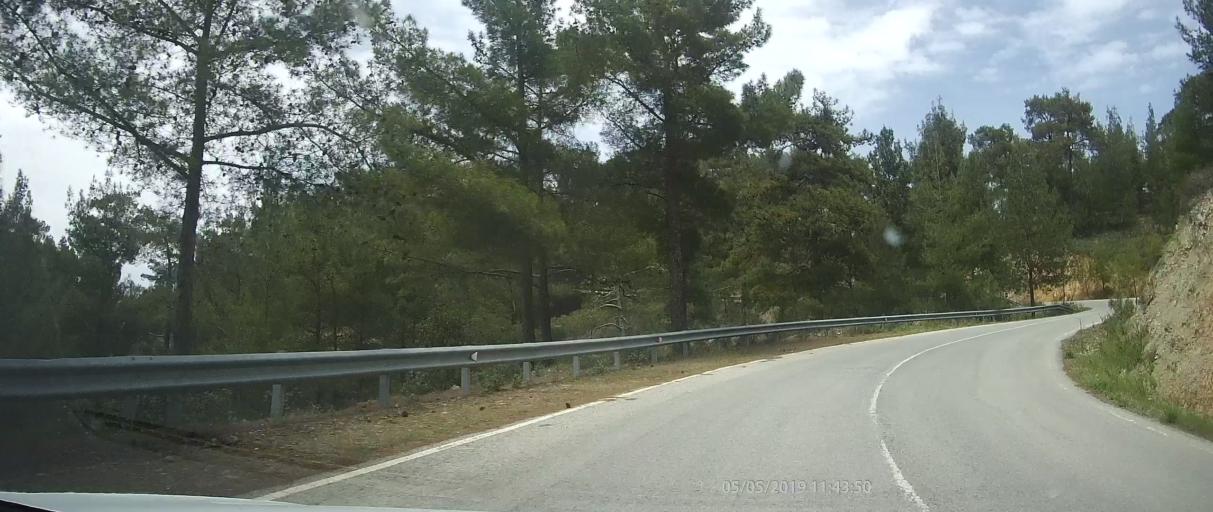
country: CY
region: Lefkosia
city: Kato Pyrgos
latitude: 35.0099
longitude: 32.6691
